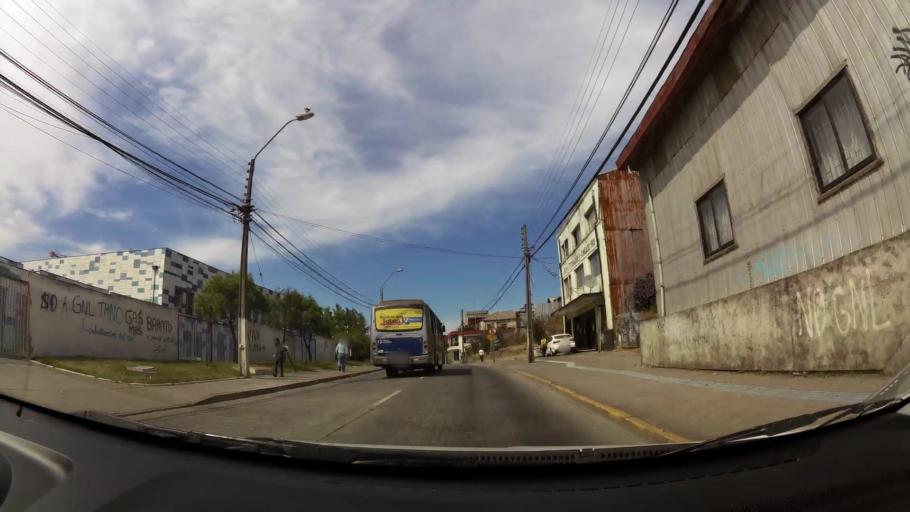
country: CL
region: Biobio
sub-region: Provincia de Concepcion
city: Talcahuano
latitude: -36.7185
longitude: -73.1101
